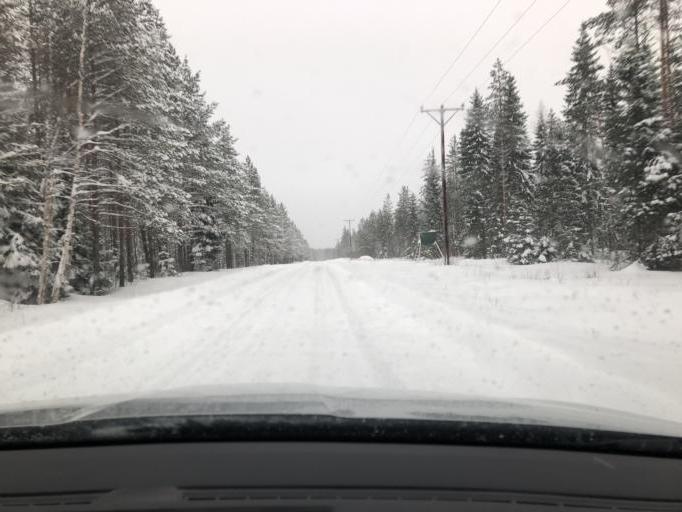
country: SE
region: Vaesterbotten
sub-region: Umea Kommun
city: Saevar
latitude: 63.9466
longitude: 20.6973
